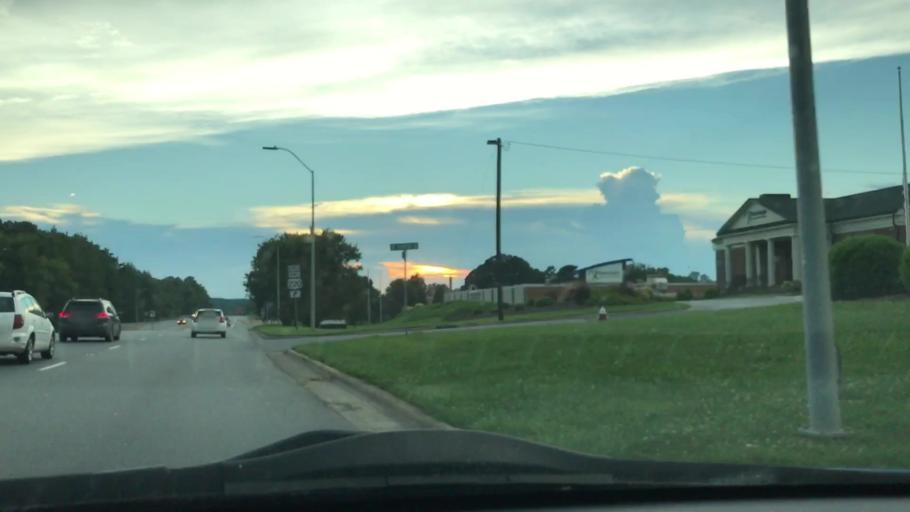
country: US
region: North Carolina
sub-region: Randolph County
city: Asheboro
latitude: 35.6887
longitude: -79.8123
